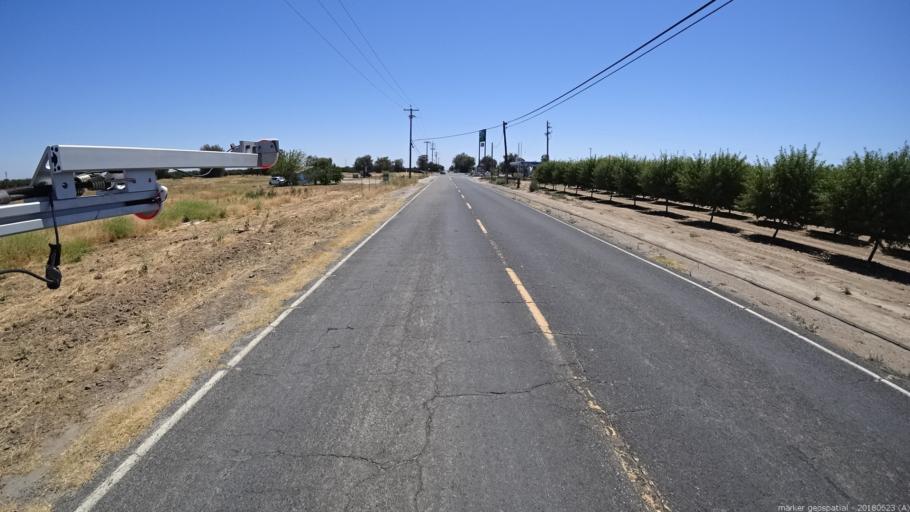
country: US
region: California
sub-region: Madera County
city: Fairmead
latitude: 37.0983
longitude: -120.2193
